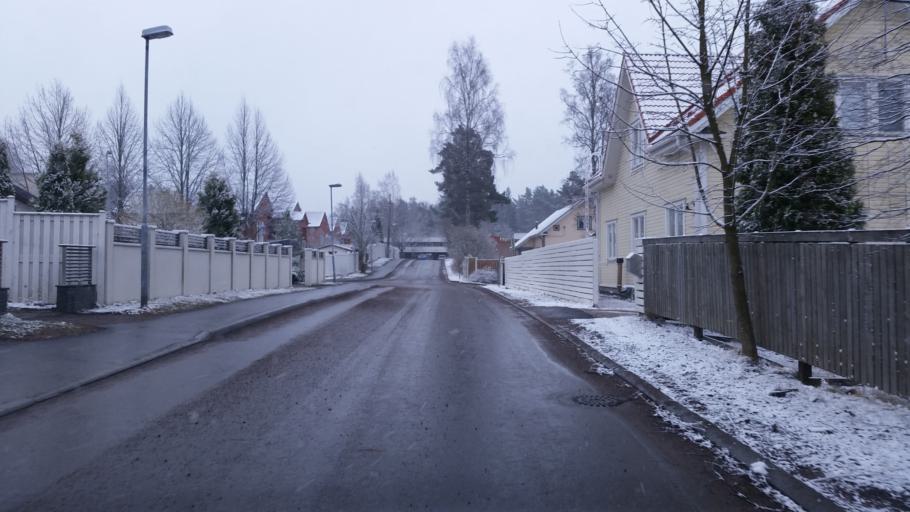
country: FI
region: Uusimaa
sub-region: Helsinki
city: Koukkuniemi
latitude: 60.1645
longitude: 24.7630
